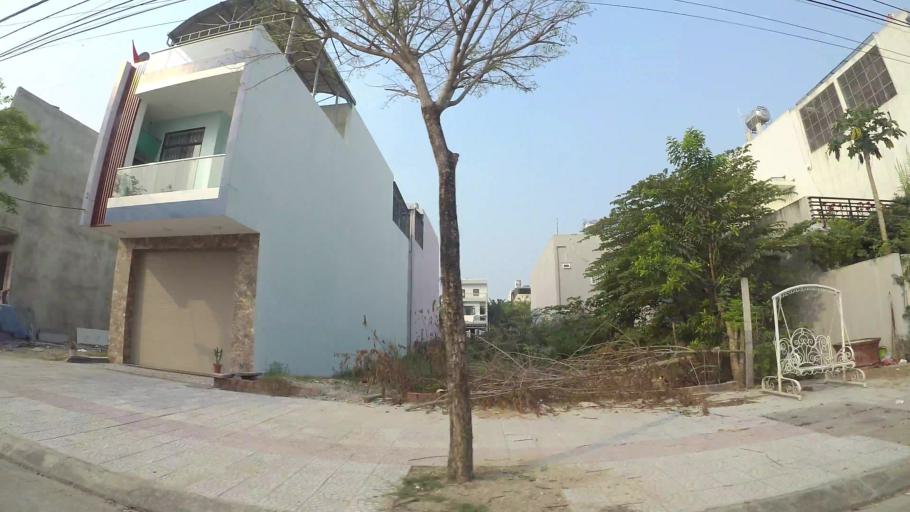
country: VN
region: Da Nang
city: Cam Le
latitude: 16.0073
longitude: 108.2228
